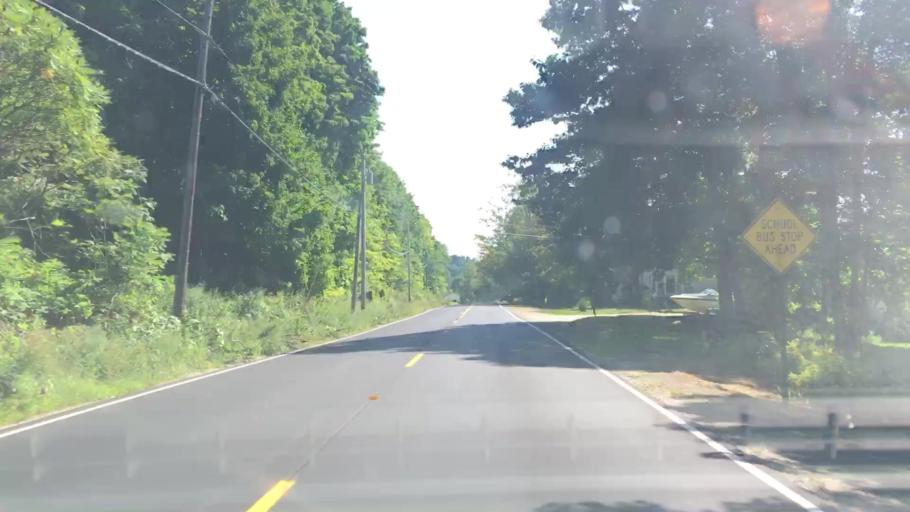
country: US
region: Maine
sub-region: Androscoggin County
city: Sabattus
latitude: 44.1336
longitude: -70.0875
